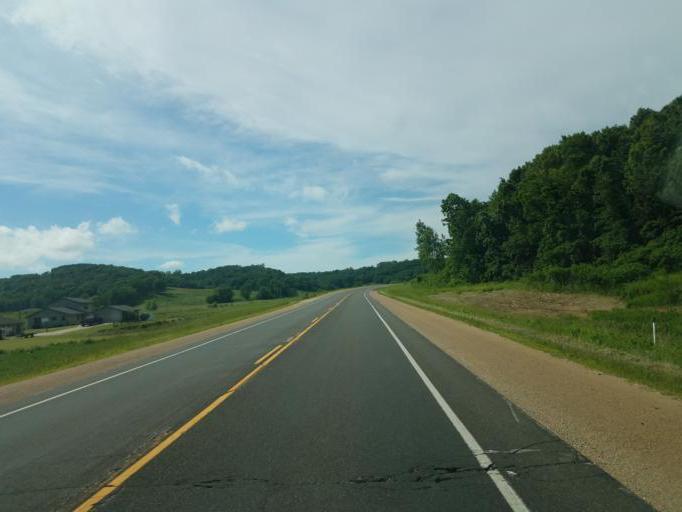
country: US
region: Wisconsin
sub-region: Monroe County
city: Tomah
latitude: 43.8737
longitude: -90.4781
